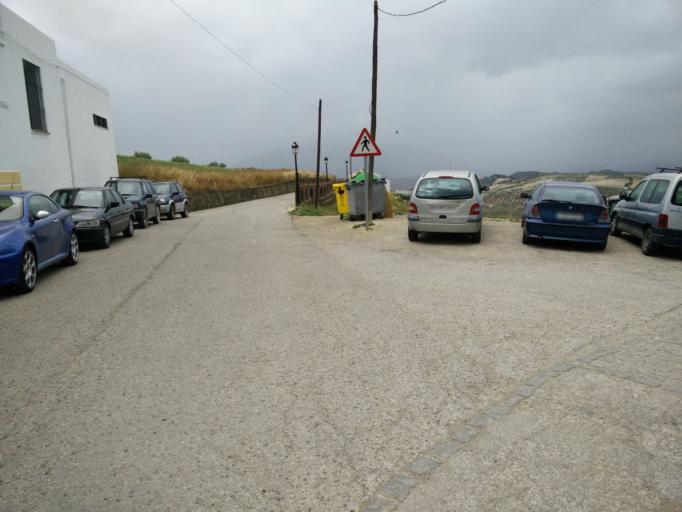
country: ES
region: Andalusia
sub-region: Provincia de Cadiz
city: Olvera
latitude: 36.9371
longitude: -5.2674
